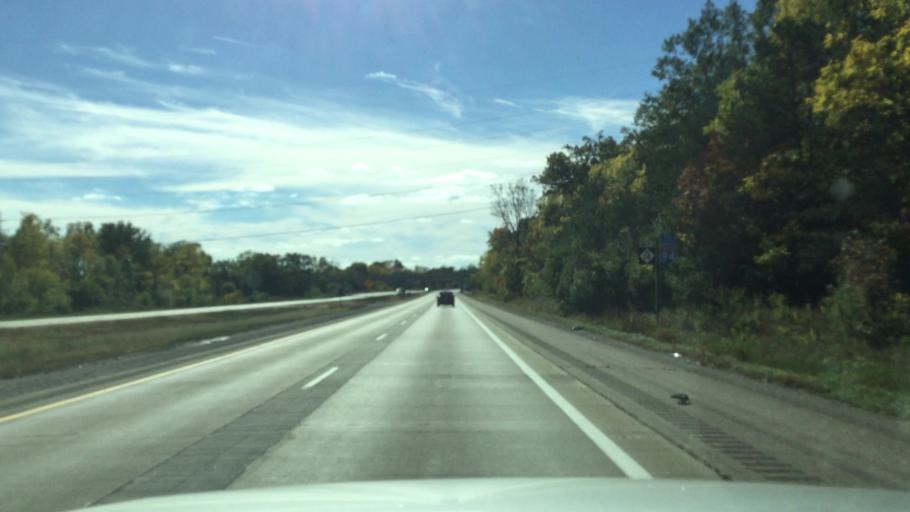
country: US
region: Michigan
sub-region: Washtenaw County
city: Ann Arbor
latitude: 42.2932
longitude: -83.7945
